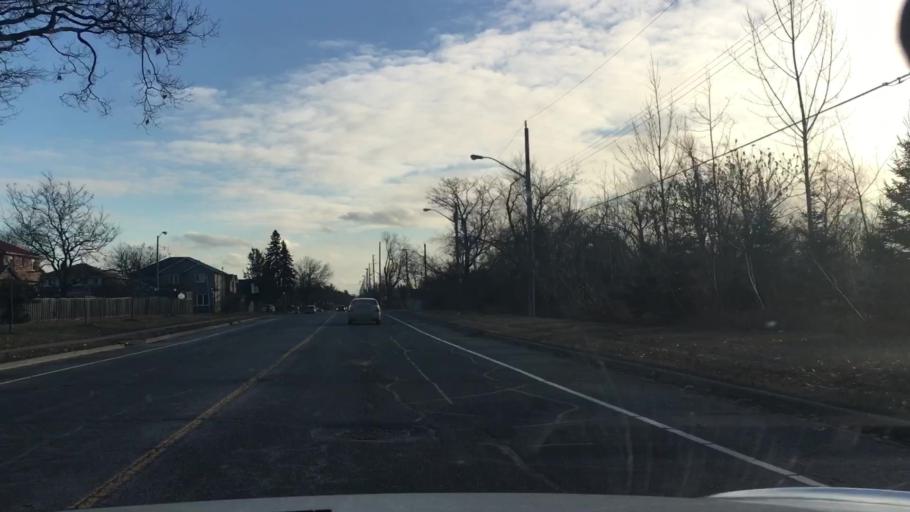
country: CA
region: Ontario
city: Scarborough
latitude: 43.7952
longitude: -79.1862
